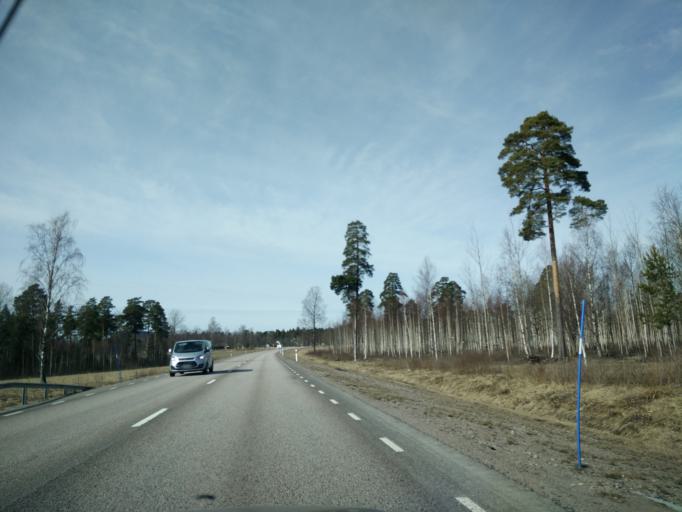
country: SE
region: Vaermland
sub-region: Hagfors Kommun
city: Hagfors
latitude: 60.0147
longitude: 13.6296
